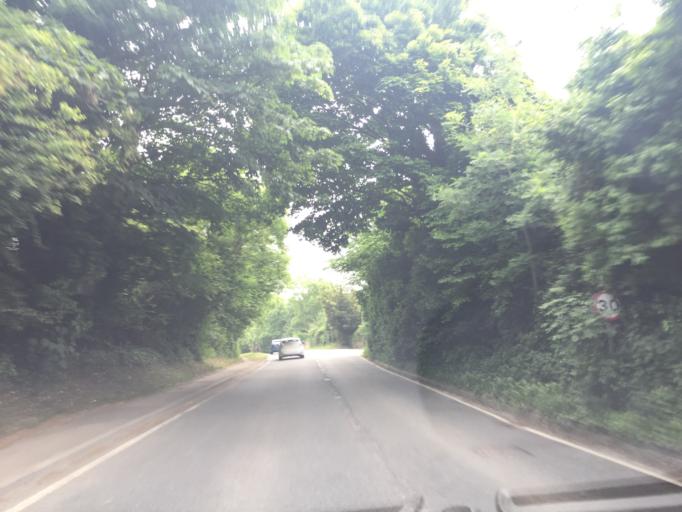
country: GB
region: England
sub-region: Dorset
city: Overcombe
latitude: 50.6451
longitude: -2.3884
